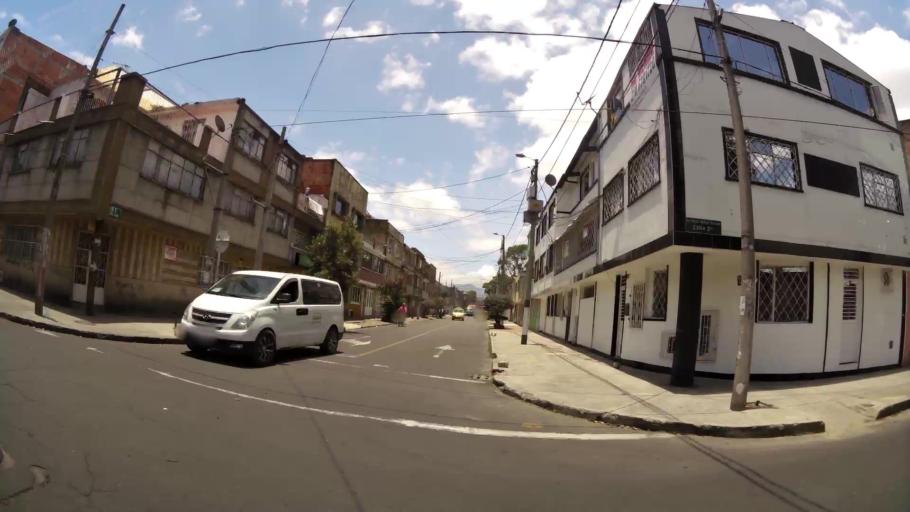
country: CO
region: Bogota D.C.
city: Bogota
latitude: 4.5908
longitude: -74.0930
